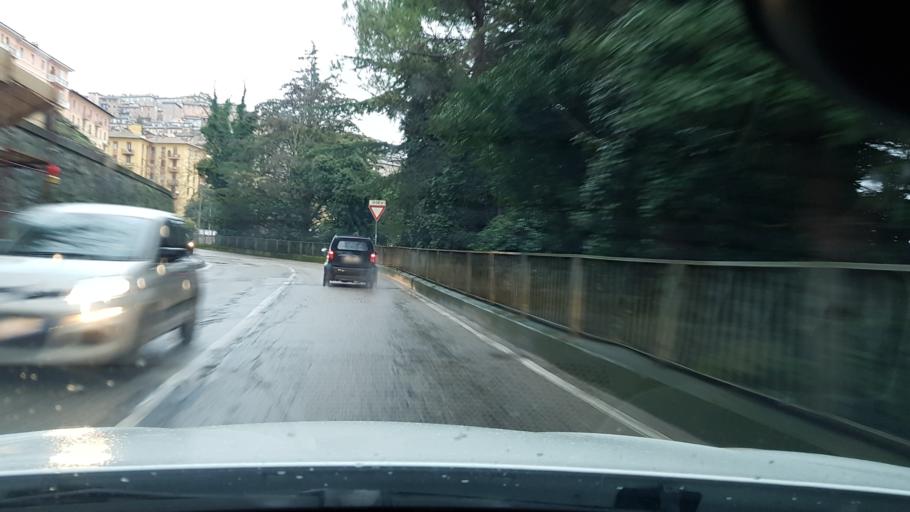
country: IT
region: Umbria
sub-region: Provincia di Perugia
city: Perugia
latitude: 43.1086
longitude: 12.3915
